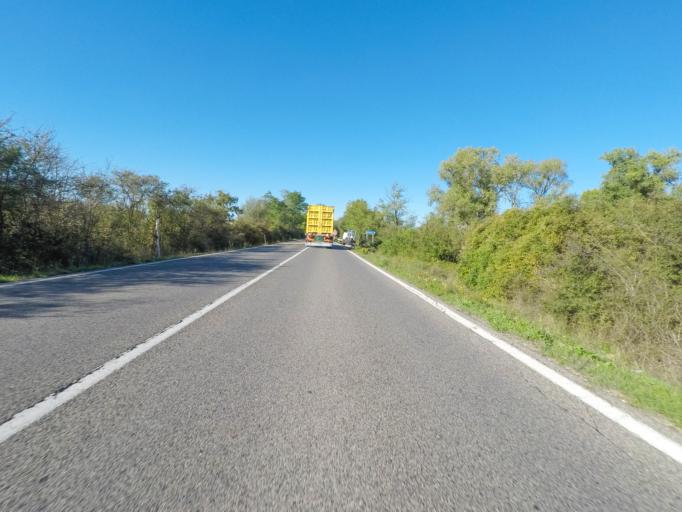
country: IT
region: Tuscany
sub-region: Provincia di Siena
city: Rosia
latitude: 43.1983
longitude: 11.2763
